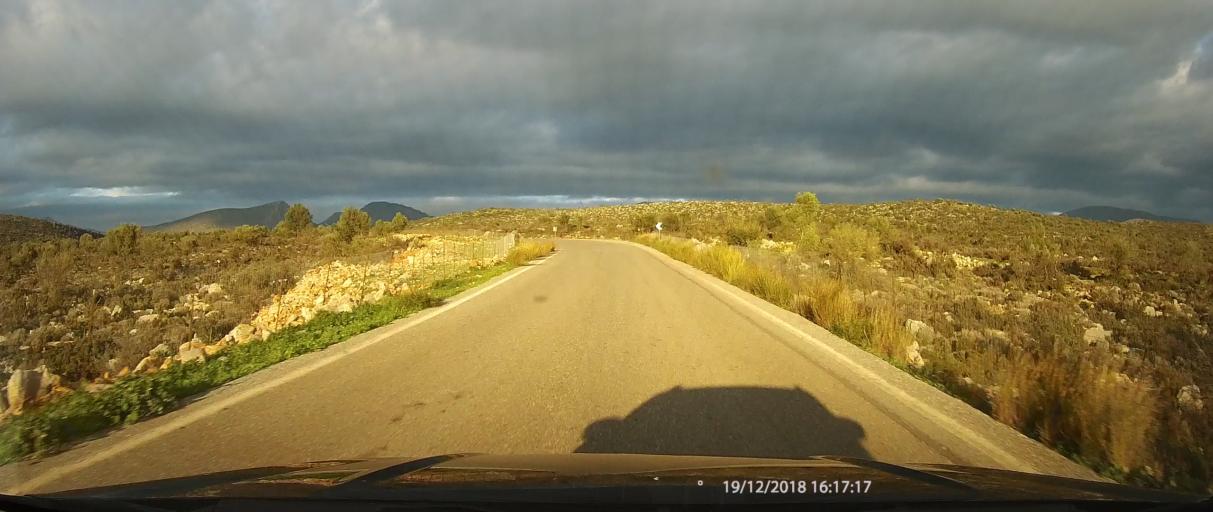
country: GR
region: Peloponnese
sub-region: Nomos Lakonias
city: Kato Glikovrisi
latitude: 36.9090
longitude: 22.8103
